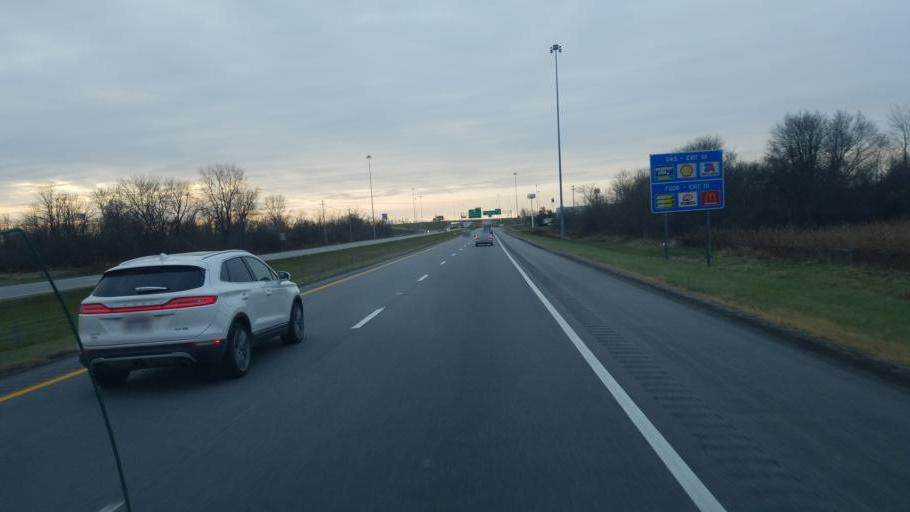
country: US
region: Ohio
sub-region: Auglaize County
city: Wapakoneta
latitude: 40.5673
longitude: -84.1703
